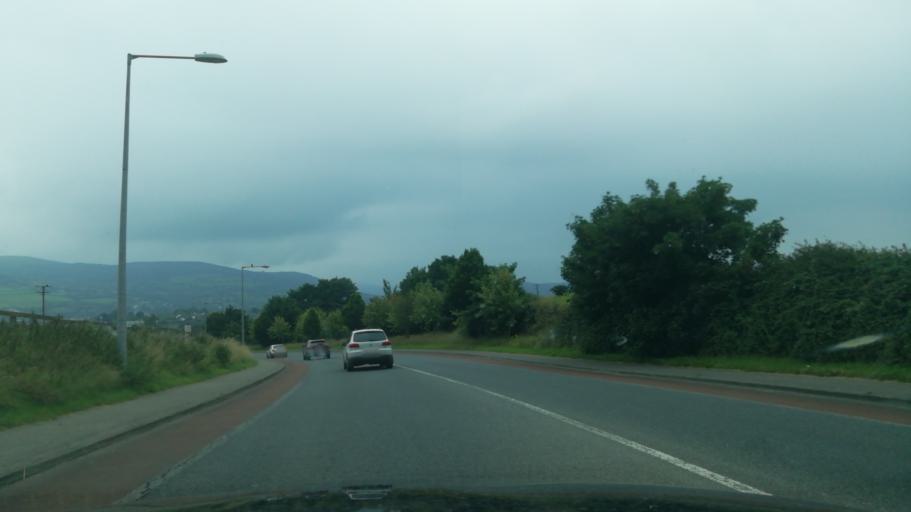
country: IE
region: Munster
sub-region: South Tipperary
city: Cluain Meala
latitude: 52.3690
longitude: -7.6999
